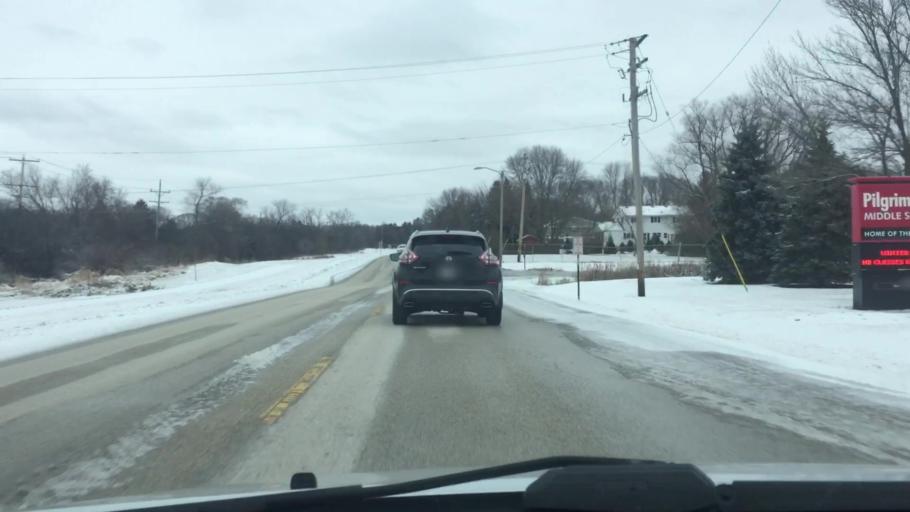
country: US
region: Wisconsin
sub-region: Waukesha County
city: Brookfield
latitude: 43.0492
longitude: -88.1059
